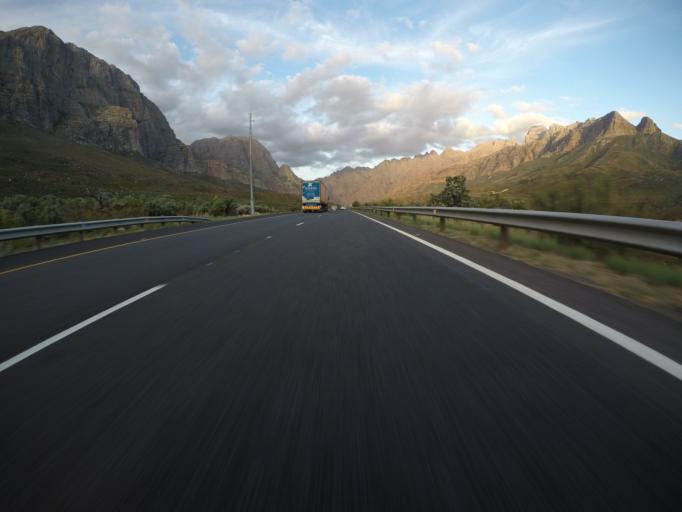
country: ZA
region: Western Cape
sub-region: Cape Winelands District Municipality
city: Paarl
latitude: -33.7263
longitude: 19.1295
